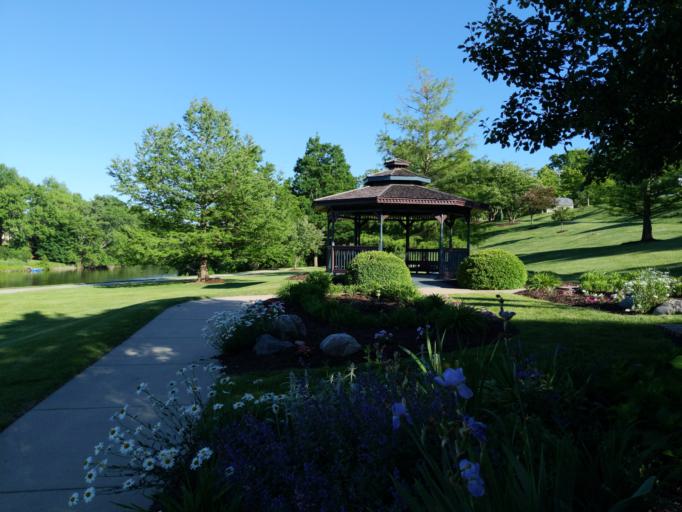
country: US
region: Michigan
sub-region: Eaton County
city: Grand Ledge
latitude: 42.7541
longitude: -84.7444
